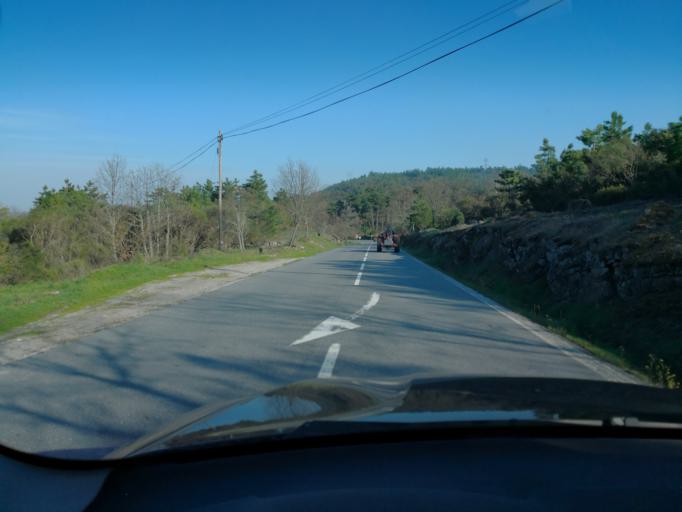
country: PT
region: Vila Real
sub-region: Sabrosa
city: Sabrosa
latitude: 41.3591
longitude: -7.6336
